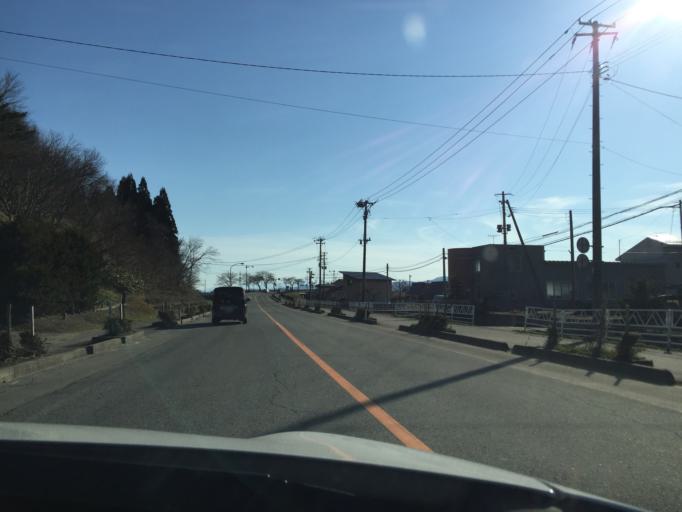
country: JP
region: Yamagata
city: Nagai
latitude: 38.1167
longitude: 140.0508
